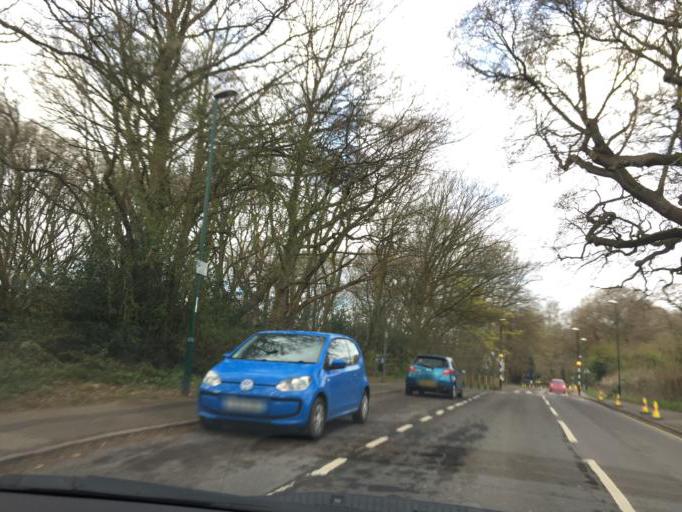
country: GB
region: England
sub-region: Coventry
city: Coventry
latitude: 52.3879
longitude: -1.5267
